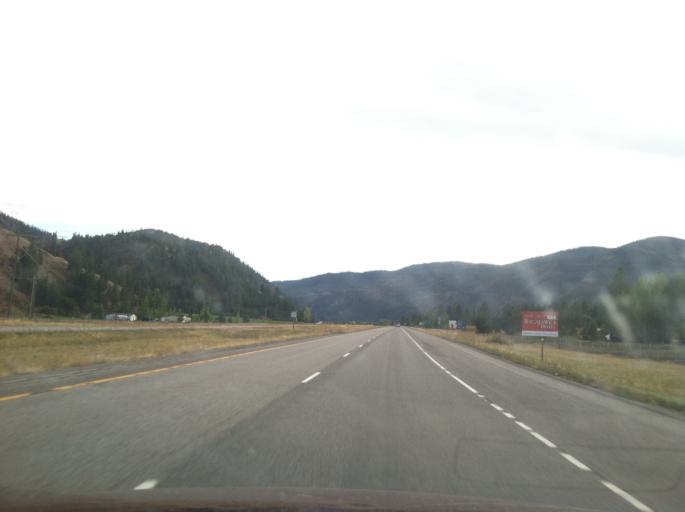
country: US
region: Montana
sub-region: Missoula County
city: Clinton
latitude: 46.7753
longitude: -113.7115
